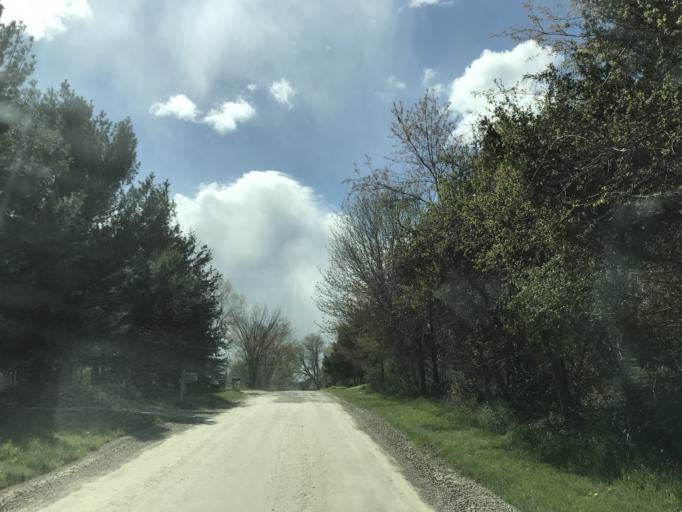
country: US
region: Michigan
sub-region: Livingston County
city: Whitmore Lake
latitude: 42.4037
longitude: -83.6907
